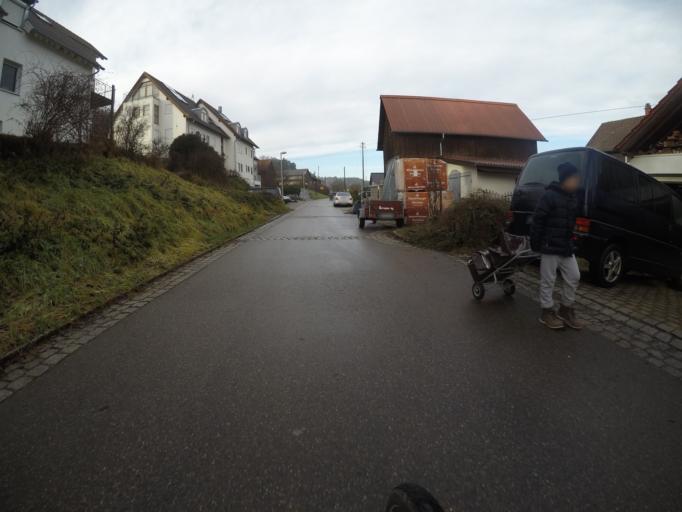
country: DE
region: Baden-Wuerttemberg
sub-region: Karlsruhe Region
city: Gechingen
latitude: 48.6772
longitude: 8.8498
